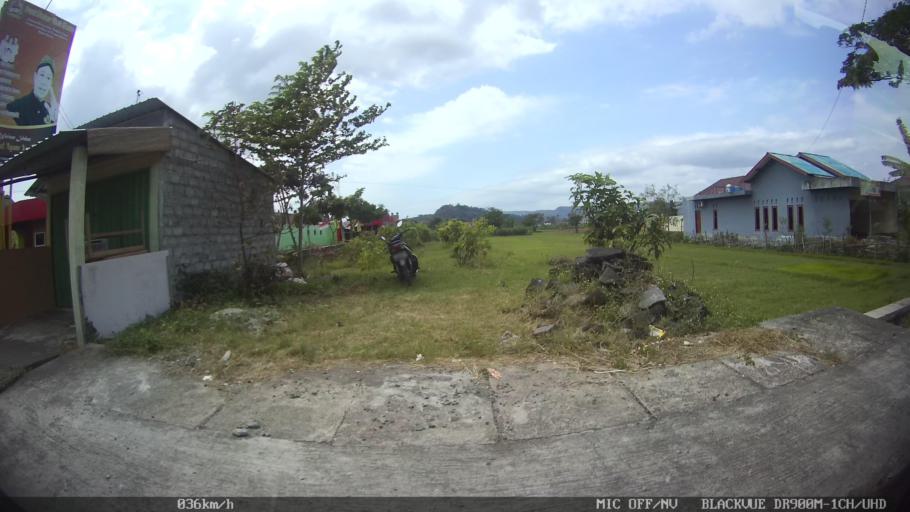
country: ID
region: Daerah Istimewa Yogyakarta
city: Depok
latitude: -7.8201
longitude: 110.4426
